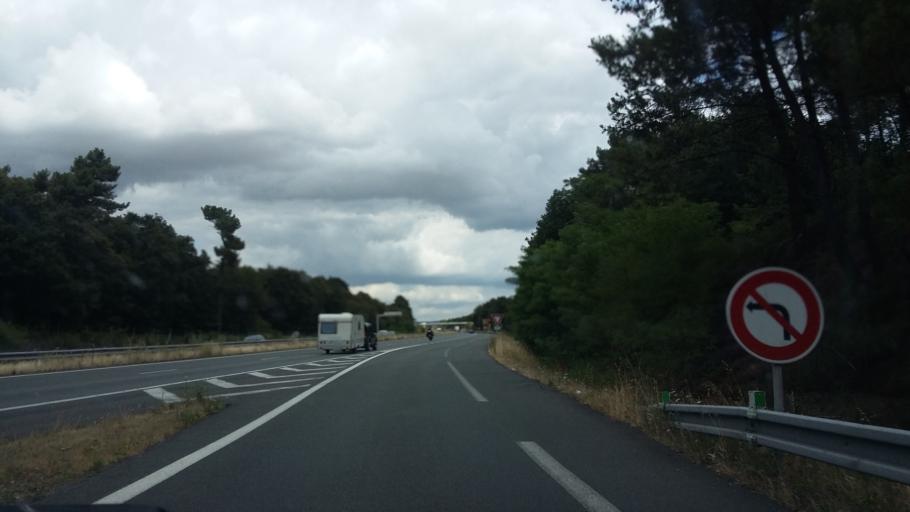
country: FR
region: Poitou-Charentes
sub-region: Departement de la Vienne
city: Chatellerault
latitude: 46.7961
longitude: 0.5116
